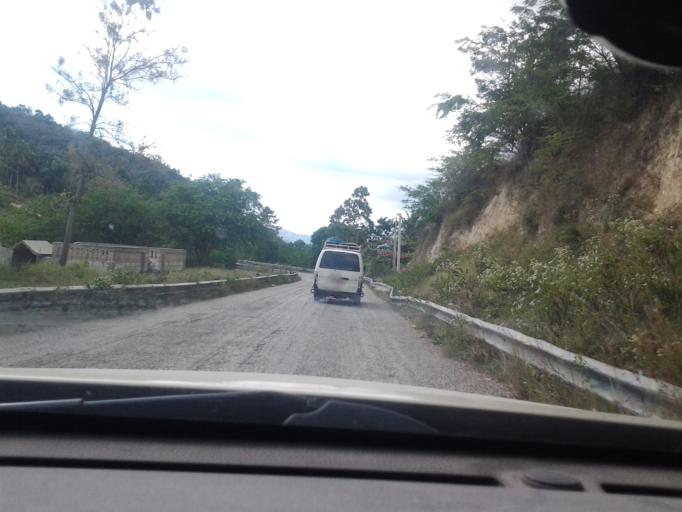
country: HT
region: Sud-Est
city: Jacmel
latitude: 18.3067
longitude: -72.5848
